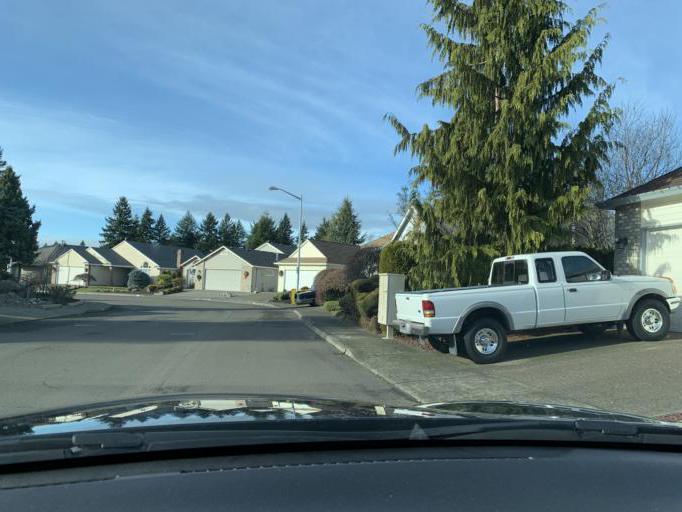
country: US
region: Washington
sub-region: Clark County
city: Mill Plain
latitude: 45.5999
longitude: -122.5079
